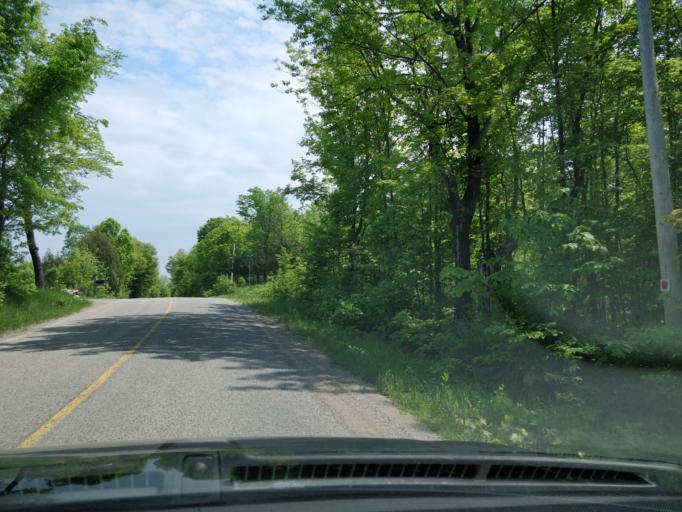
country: CA
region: Ontario
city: Perth
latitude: 44.6571
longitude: -76.5643
